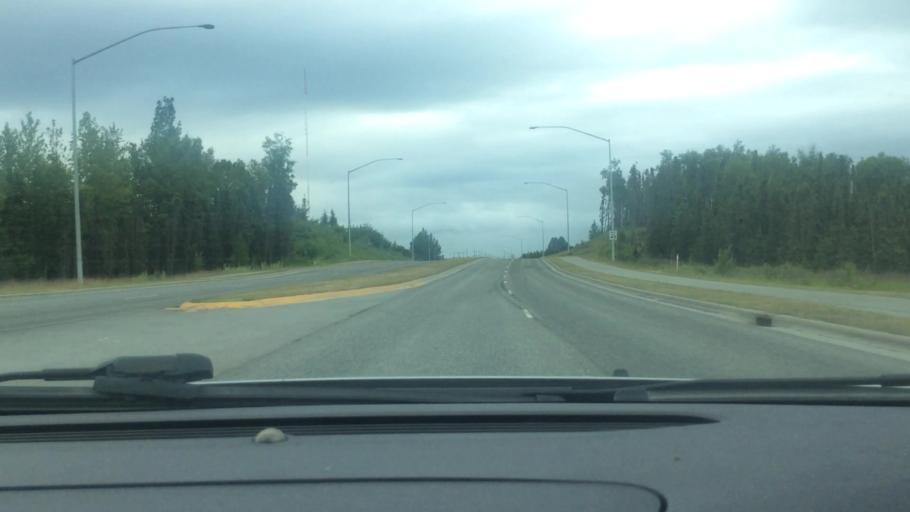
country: US
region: Alaska
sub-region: Anchorage Municipality
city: Anchorage
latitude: 61.1667
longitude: -149.8189
